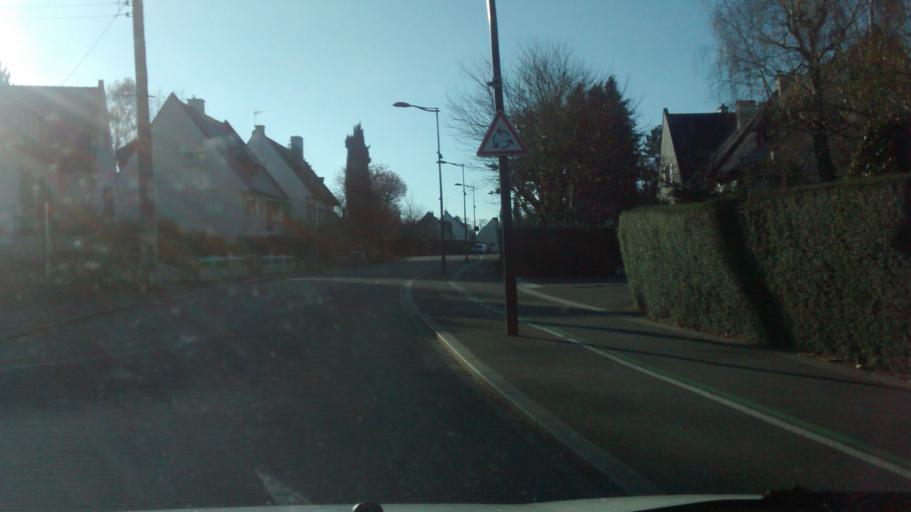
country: FR
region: Brittany
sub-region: Departement d'Ille-et-Vilaine
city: Pace
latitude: 48.1514
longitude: -1.7706
